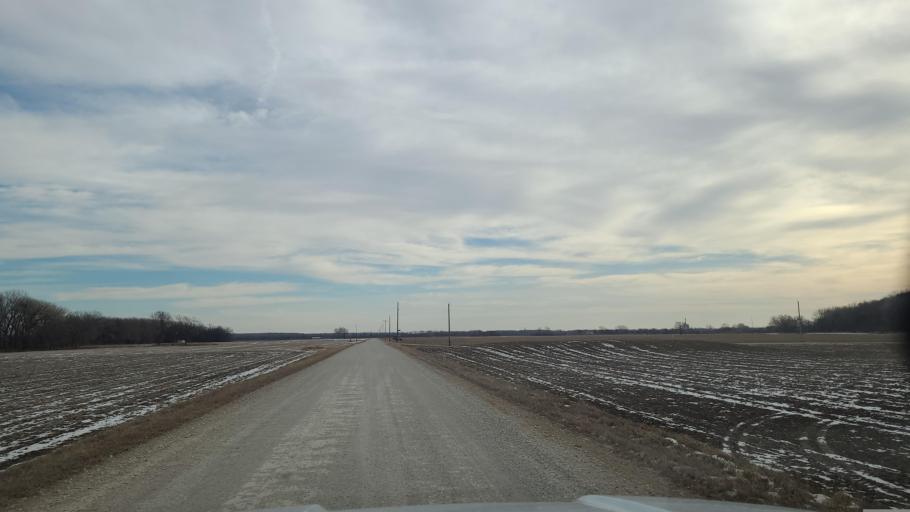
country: US
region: Kansas
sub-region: Douglas County
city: Lawrence
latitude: 39.0297
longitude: -95.3281
